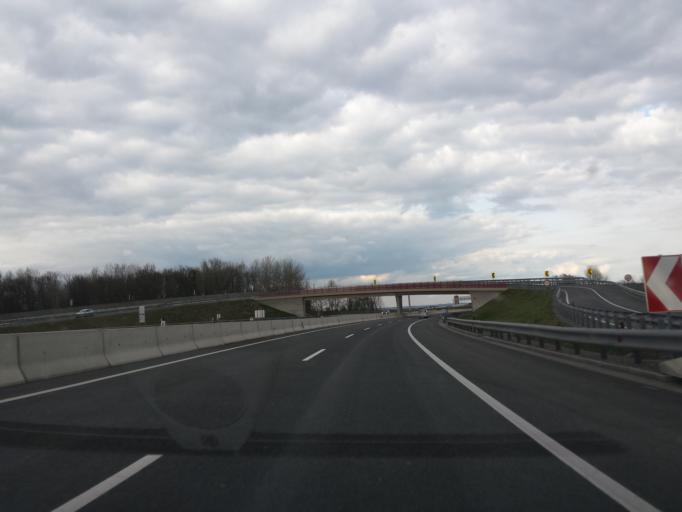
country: AT
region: Lower Austria
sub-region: Politischer Bezirk Krems
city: Grafenegg
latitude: 48.4078
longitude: 15.7438
